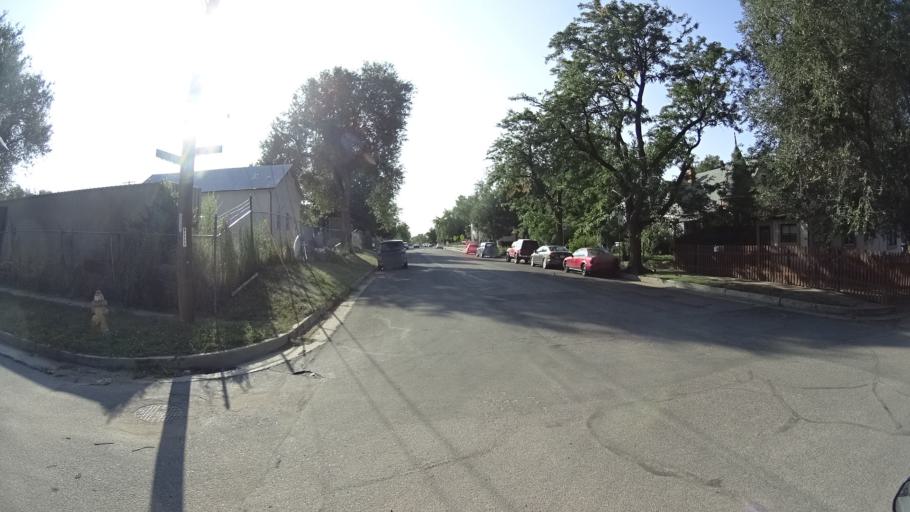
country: US
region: Colorado
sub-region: El Paso County
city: Colorado Springs
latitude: 38.8492
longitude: -104.8679
